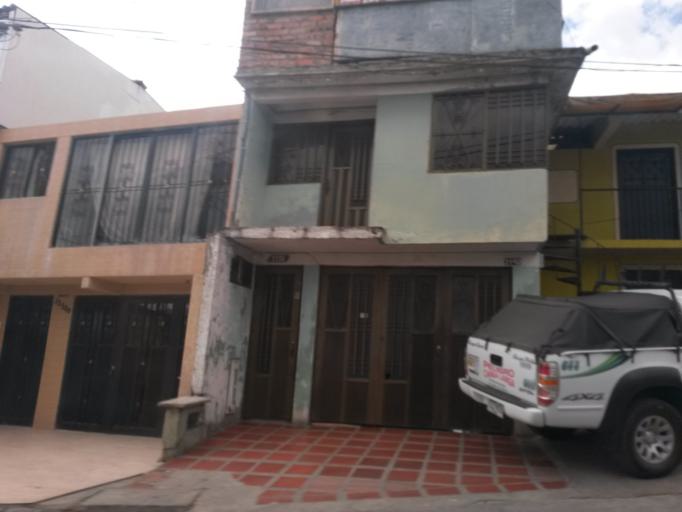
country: CO
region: Cauca
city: Popayan
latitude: 2.4471
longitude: -76.6287
